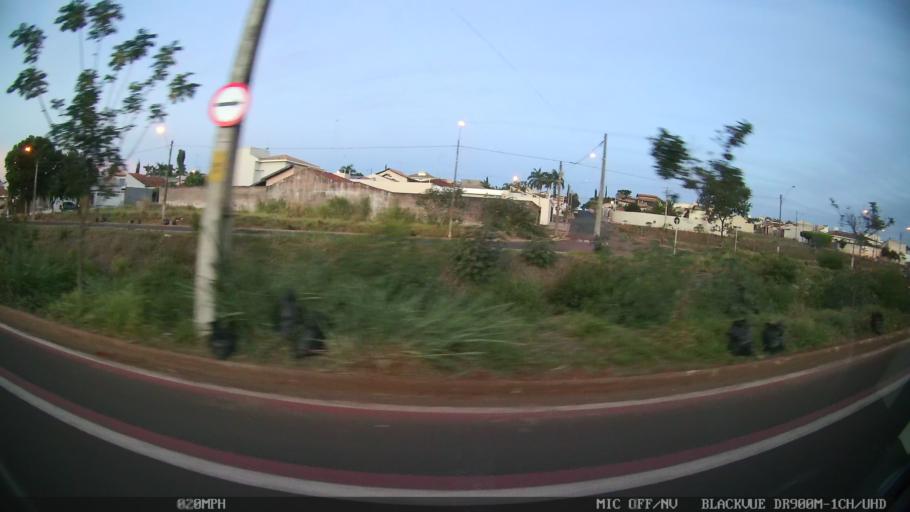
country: BR
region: Sao Paulo
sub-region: Catanduva
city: Catanduva
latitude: -21.1458
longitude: -48.9916
